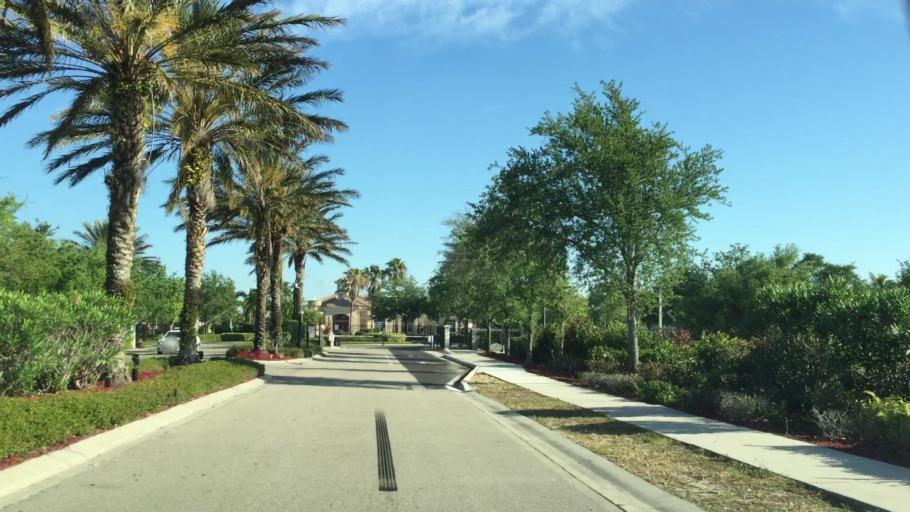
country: US
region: Florida
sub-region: Lee County
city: Gateway
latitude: 26.6212
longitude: -81.7608
